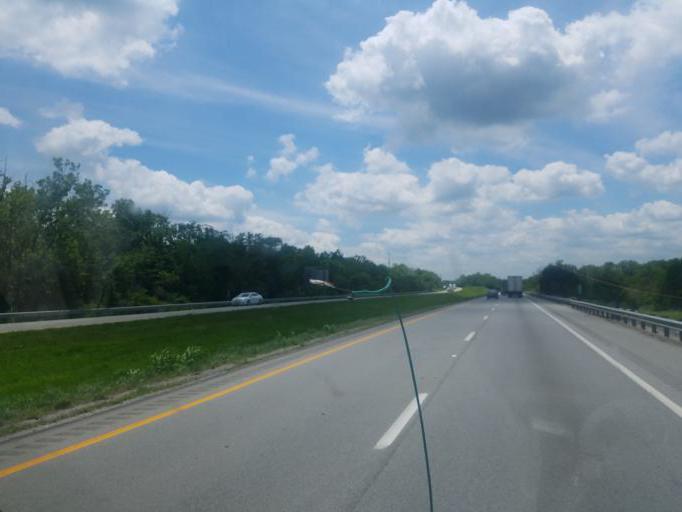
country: US
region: Kentucky
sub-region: Trimble County
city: Providence
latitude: 38.4916
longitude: -85.2591
